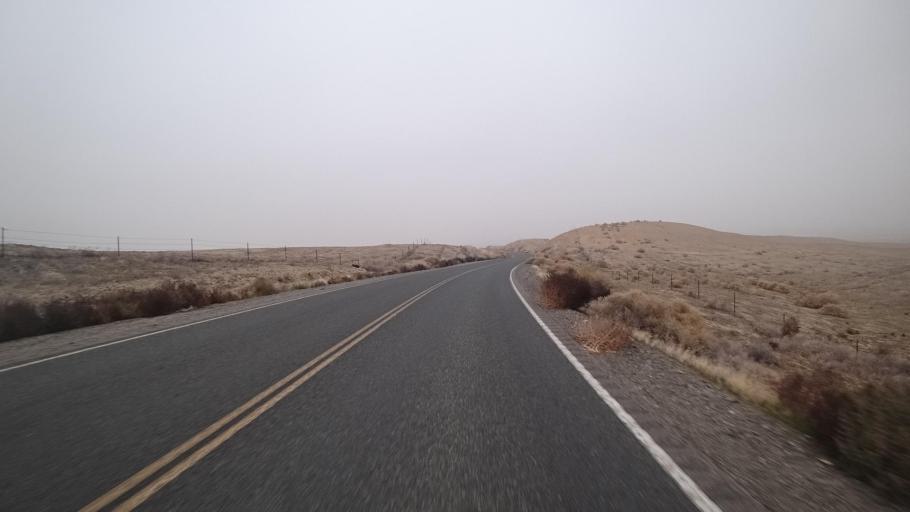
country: US
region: California
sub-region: Kern County
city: Buttonwillow
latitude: 35.3209
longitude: -119.4650
